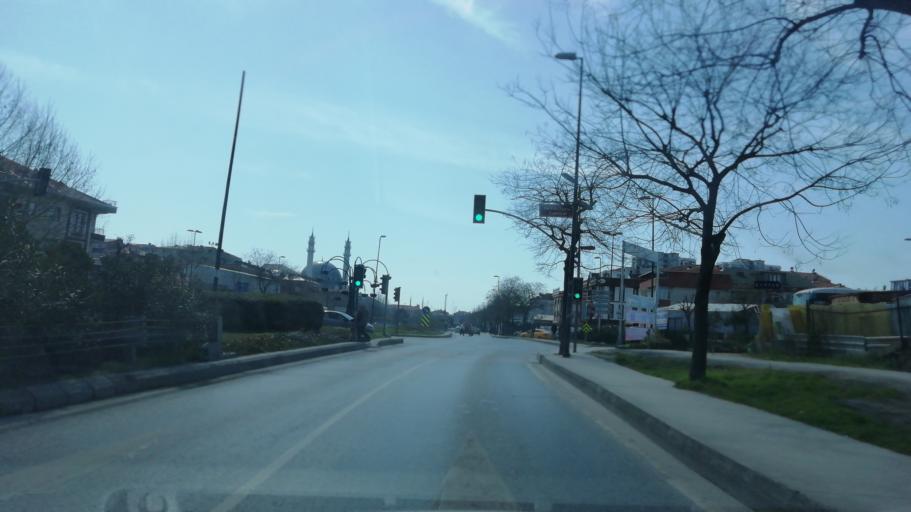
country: TR
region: Istanbul
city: Bahcelievler
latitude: 41.0173
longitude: 28.8487
